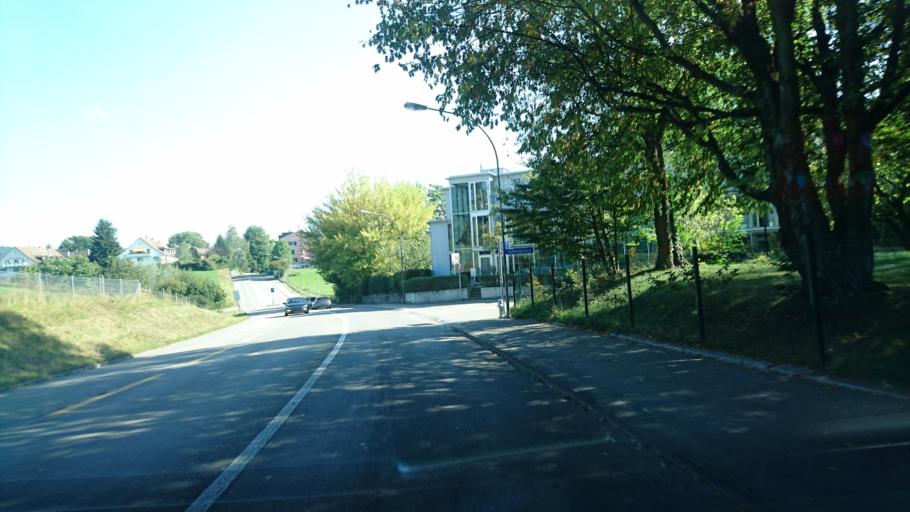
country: CH
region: Bern
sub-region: Bern-Mittelland District
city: Bern
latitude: 46.9471
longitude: 7.4668
